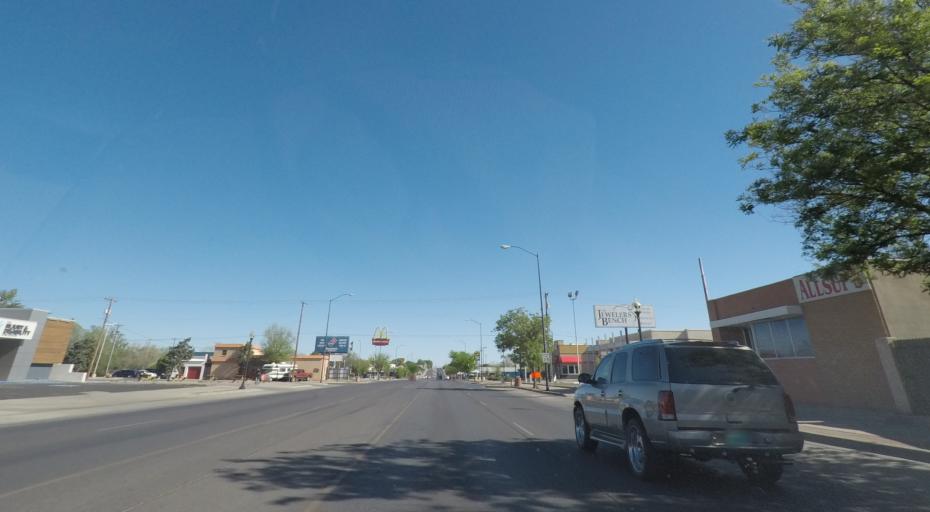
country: US
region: New Mexico
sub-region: Chaves County
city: Roswell
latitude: 33.3992
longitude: -104.5228
